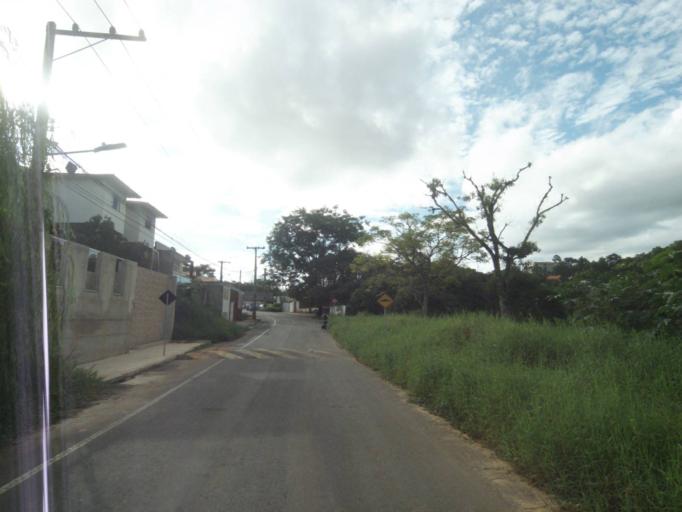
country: BR
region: Parana
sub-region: Telemaco Borba
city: Telemaco Borba
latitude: -24.3353
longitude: -50.6112
